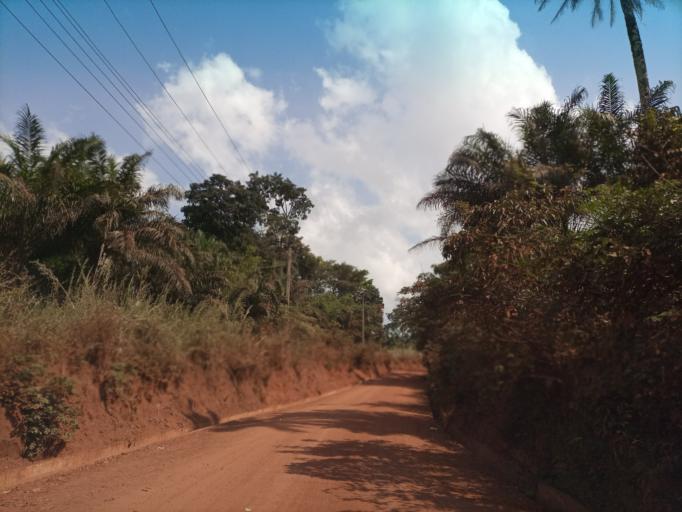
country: NG
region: Enugu
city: Oji River
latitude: 6.3090
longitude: 7.3054
